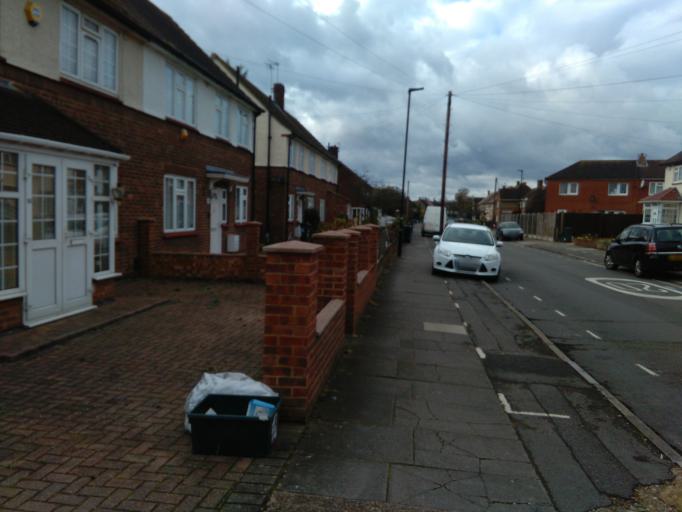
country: GB
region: England
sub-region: Greater London
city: Feltham
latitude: 51.4486
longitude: -0.4366
